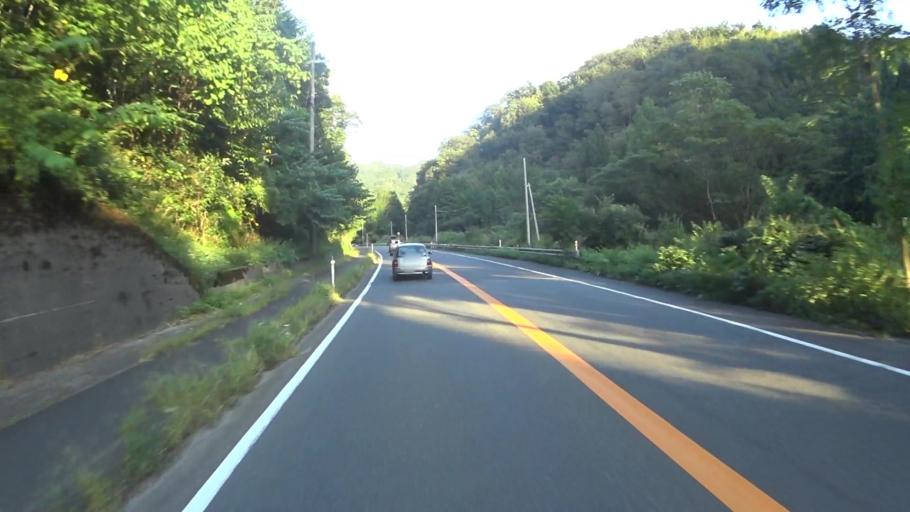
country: JP
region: Kyoto
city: Miyazu
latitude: 35.5614
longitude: 135.1073
